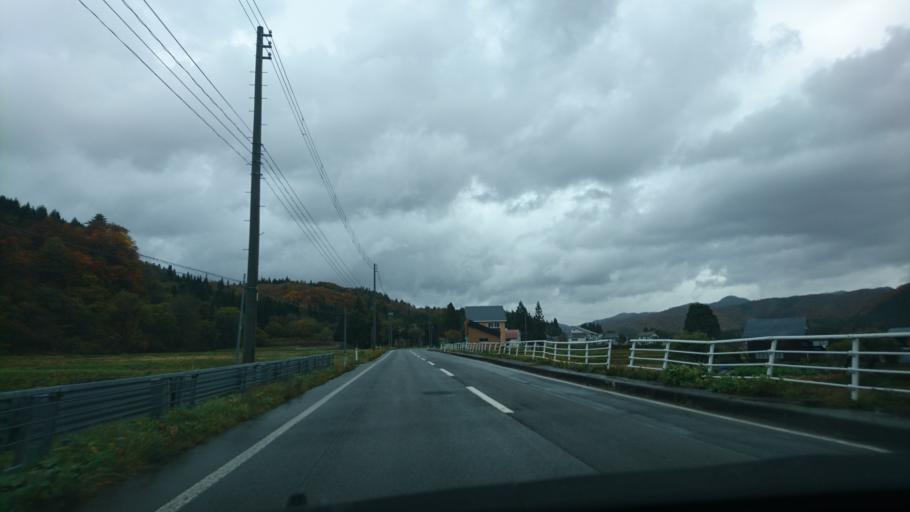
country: JP
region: Akita
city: Kakunodatemachi
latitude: 39.4865
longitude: 140.8061
